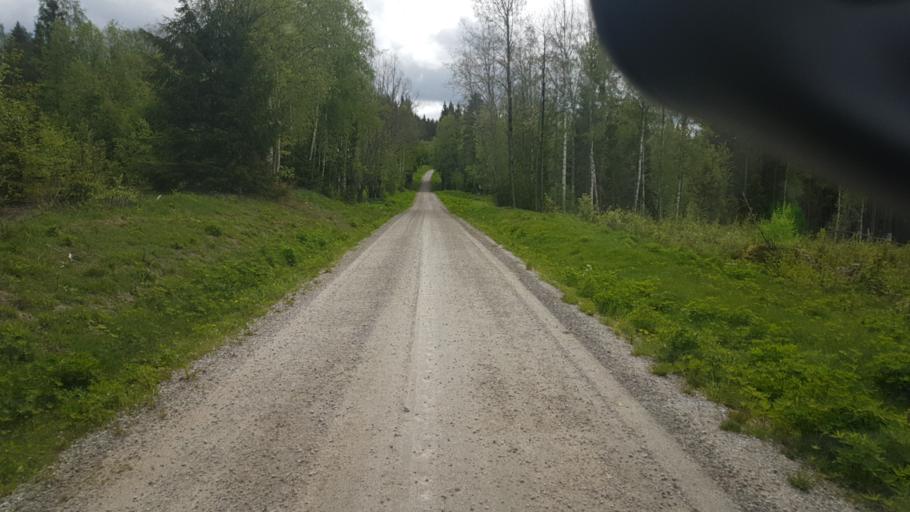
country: SE
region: Vaermland
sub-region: Arvika Kommun
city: Arvika
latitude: 59.8391
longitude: 12.7587
